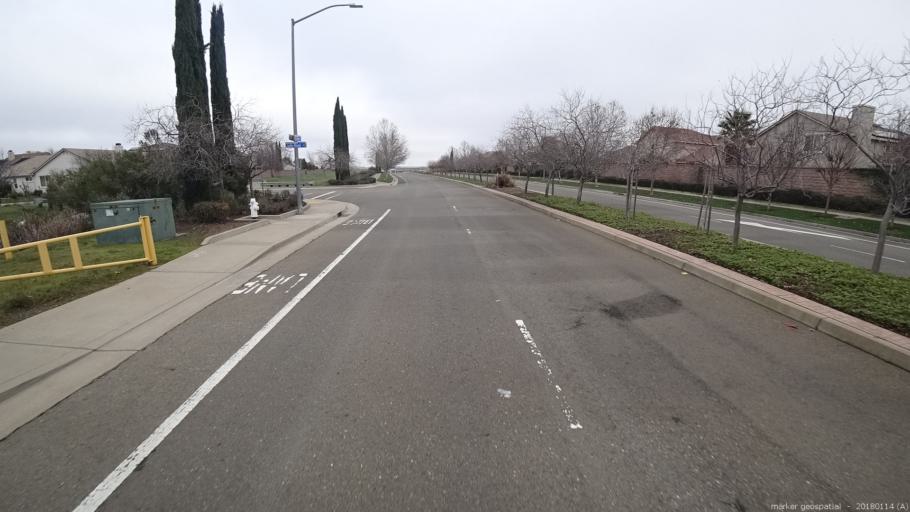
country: US
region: California
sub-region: Sacramento County
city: Rancho Cordova
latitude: 38.5489
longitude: -121.2357
